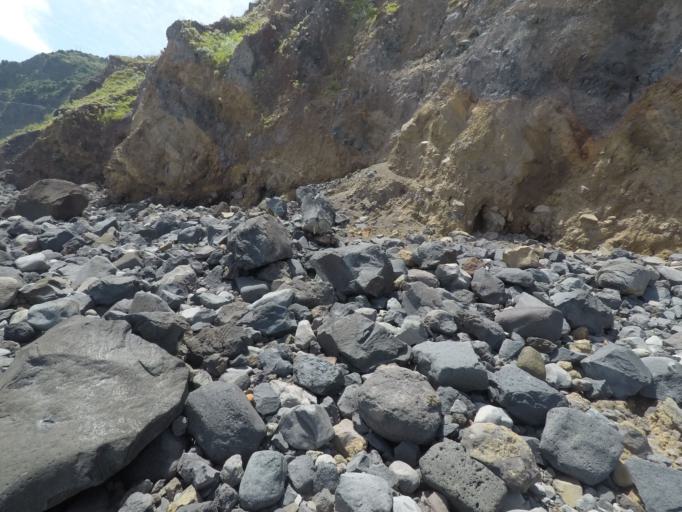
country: PT
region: Madeira
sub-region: Sao Vicente
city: Sao Vicente
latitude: 32.8301
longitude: -16.9877
